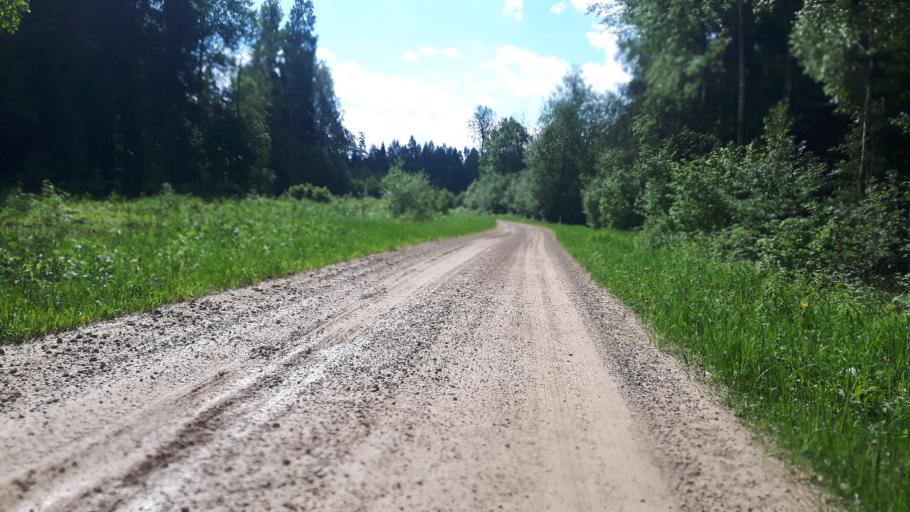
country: EE
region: Paernumaa
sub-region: Vaendra vald (alev)
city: Vandra
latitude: 58.7112
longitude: 25.0440
